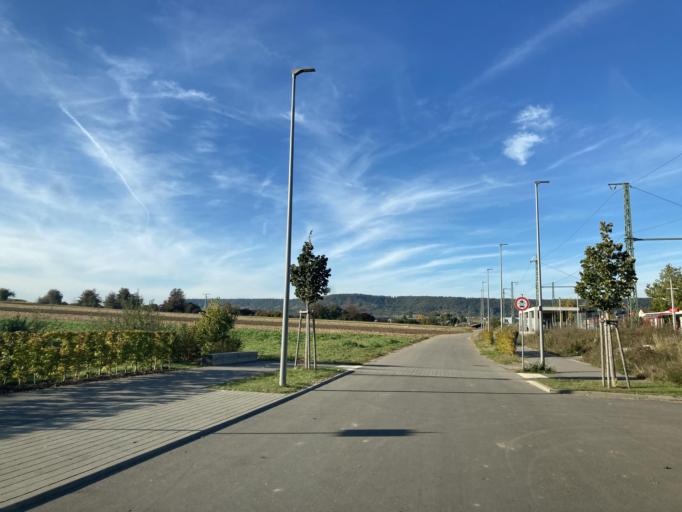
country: DE
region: Baden-Wuerttemberg
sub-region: Regierungsbezirk Stuttgart
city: Hildrizhausen
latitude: 48.5516
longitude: 8.9629
